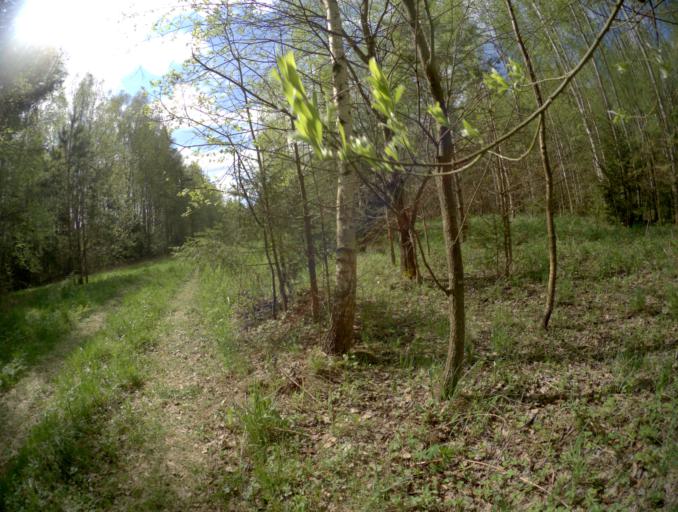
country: RU
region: Vladimir
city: Golovino
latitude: 55.9913
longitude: 40.4096
